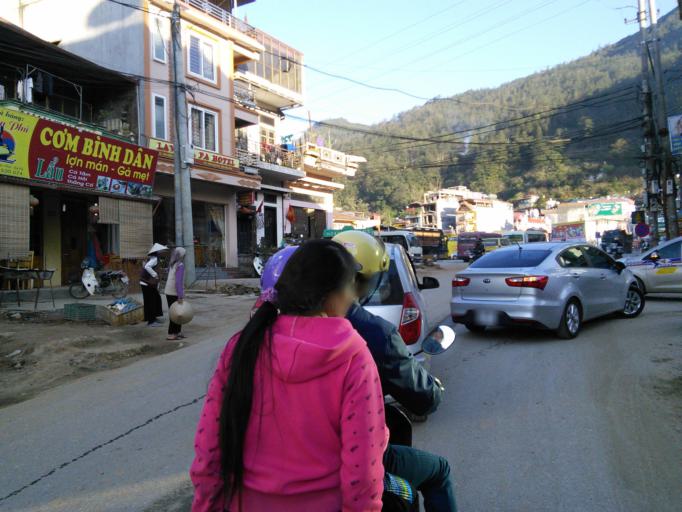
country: VN
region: Lao Cai
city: Sa Pa
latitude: 22.3389
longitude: 103.8508
